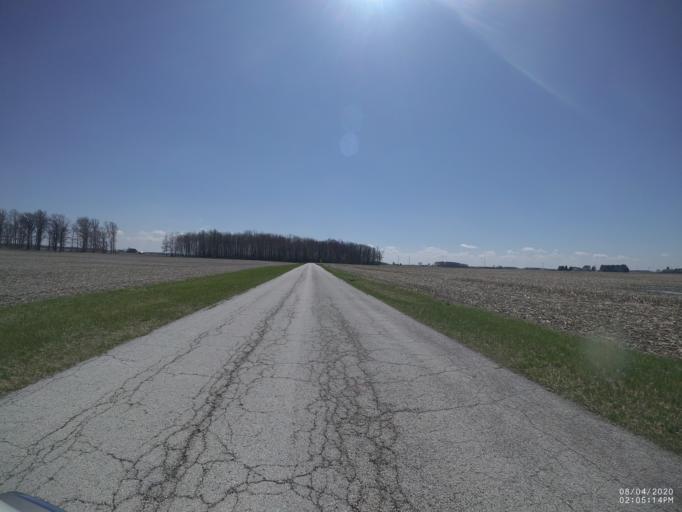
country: US
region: Ohio
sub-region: Sandusky County
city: Gibsonburg
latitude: 41.2927
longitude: -83.2957
